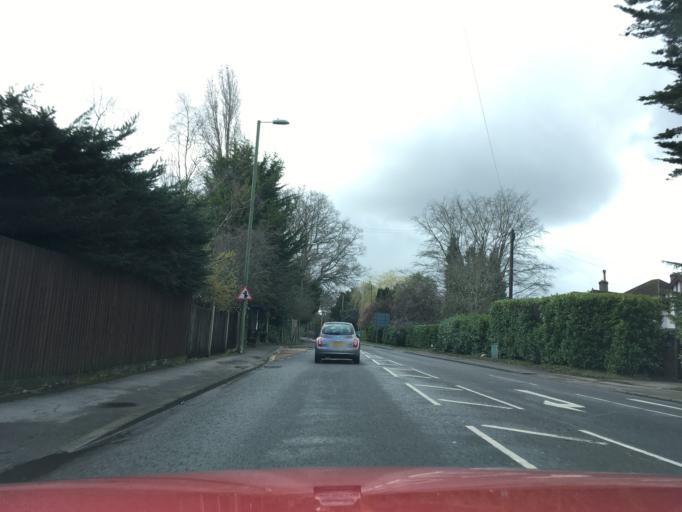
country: GB
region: England
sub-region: Hampshire
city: Chandlers Ford
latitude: 50.9746
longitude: -1.3883
